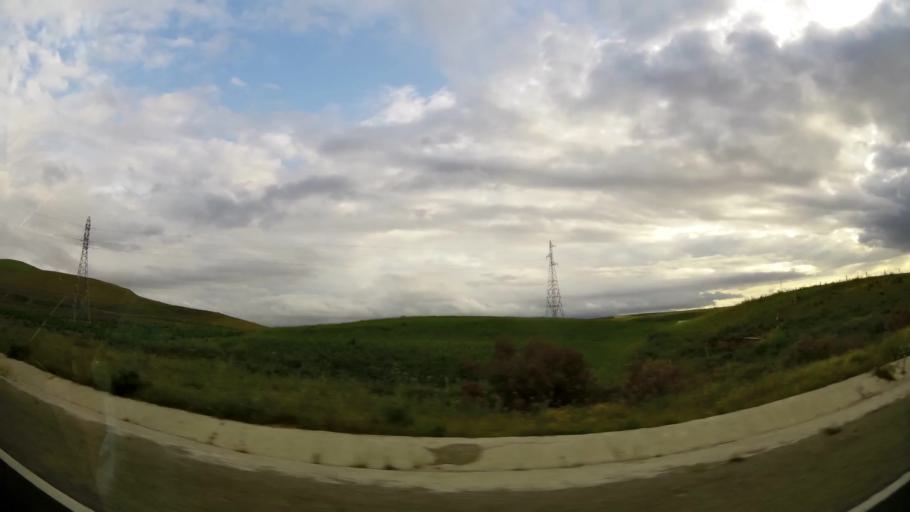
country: MA
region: Taza-Al Hoceima-Taounate
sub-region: Taza
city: Taza
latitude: 34.2582
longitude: -3.9357
